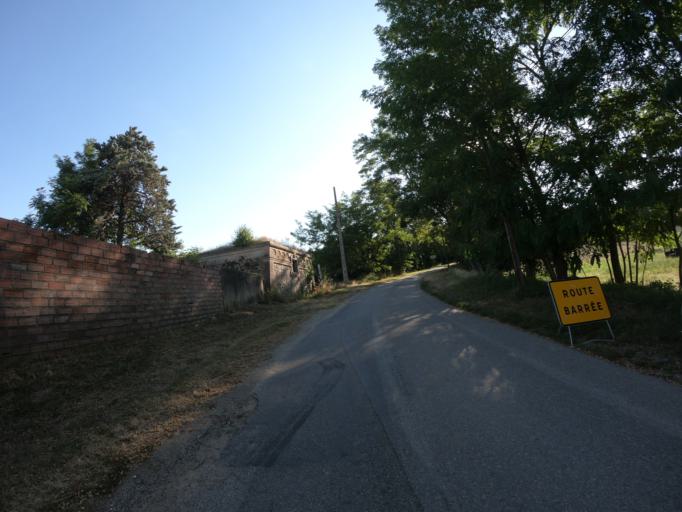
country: FR
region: Midi-Pyrenees
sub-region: Departement de l'Ariege
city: La Tour-du-Crieu
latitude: 43.1103
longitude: 1.7210
